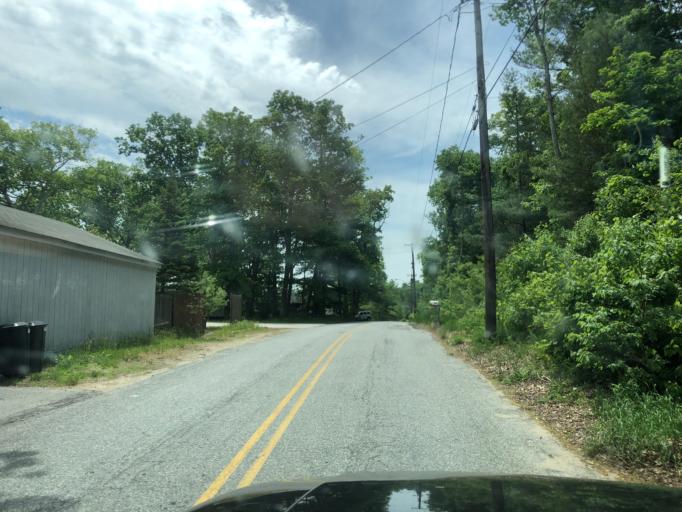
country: US
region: Connecticut
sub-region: Windham County
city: Thompson
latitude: 41.9587
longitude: -71.8219
